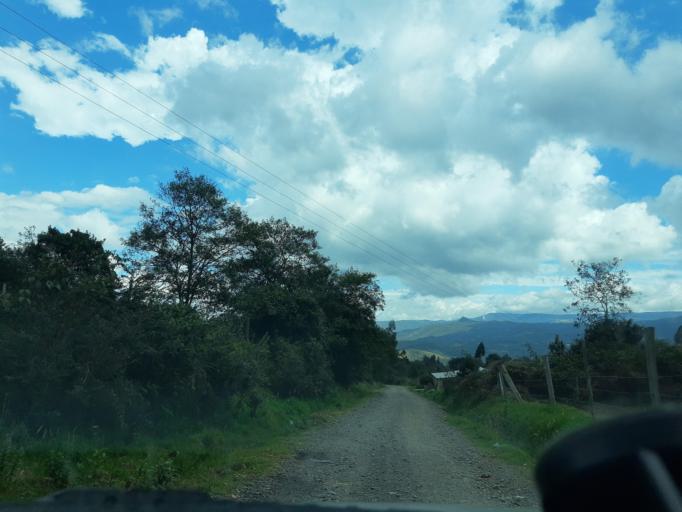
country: CO
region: Boyaca
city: Raquira
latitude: 5.5080
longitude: -73.6812
